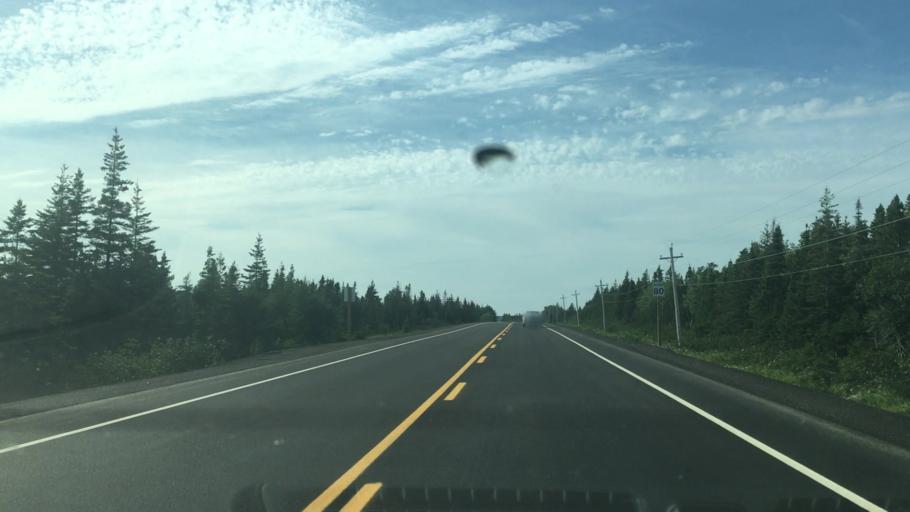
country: CA
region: Nova Scotia
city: Sydney Mines
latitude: 46.8460
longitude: -60.4105
